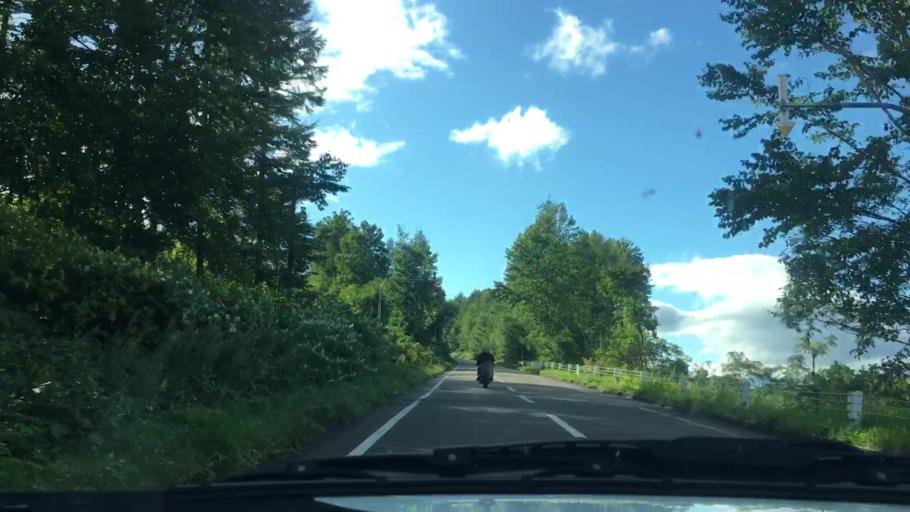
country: JP
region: Hokkaido
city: Otofuke
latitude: 43.1716
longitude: 142.9751
